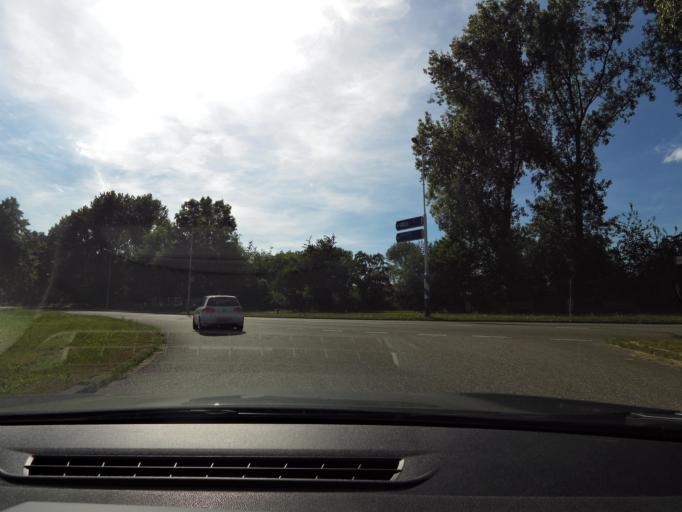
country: NL
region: South Holland
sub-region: Gemeente Rotterdam
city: Delfshaven
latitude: 51.8790
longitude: 4.4662
